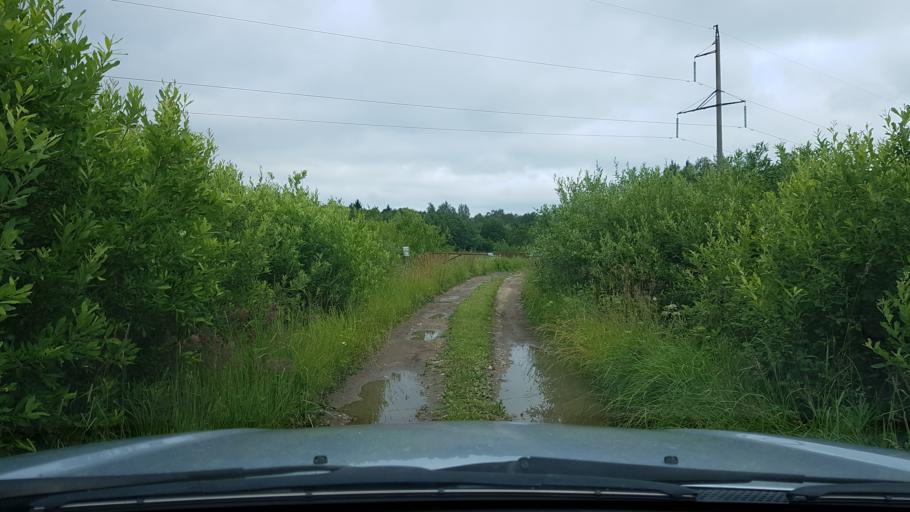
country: EE
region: Ida-Virumaa
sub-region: Narva-Joesuu linn
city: Narva-Joesuu
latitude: 59.3654
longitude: 28.0444
